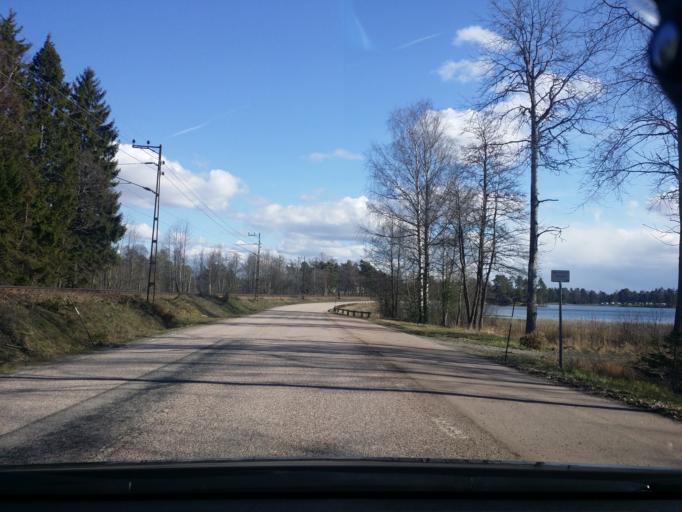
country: SE
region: Vaestmanland
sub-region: Sala Kommun
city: Sala
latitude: 59.9633
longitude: 16.5108
